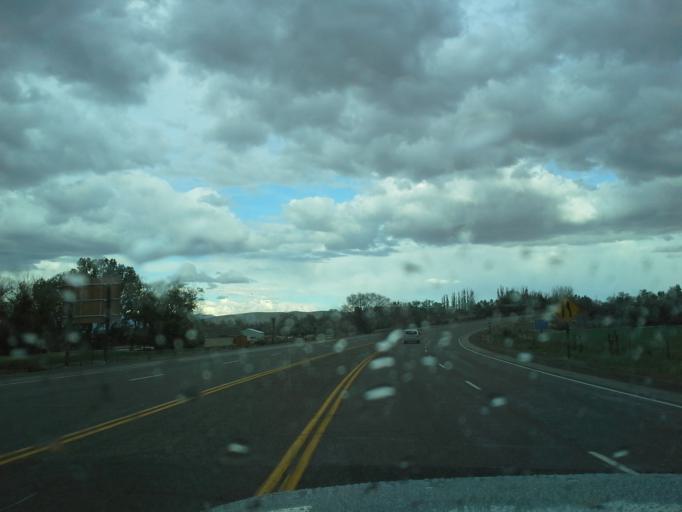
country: US
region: Wyoming
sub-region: Big Horn County
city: Lovell
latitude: 44.8368
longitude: -108.3786
